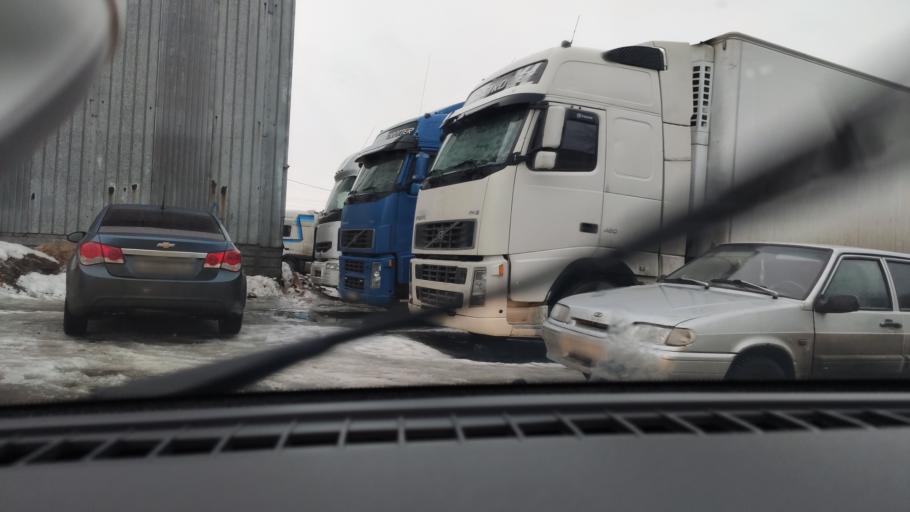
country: RU
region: Samara
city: Petra-Dubrava
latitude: 53.2538
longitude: 50.2915
